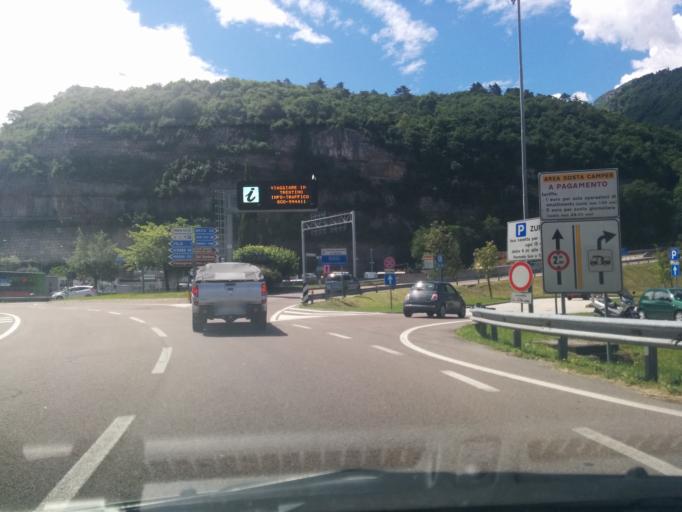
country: IT
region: Trentino-Alto Adige
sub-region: Provincia di Trento
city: Trento
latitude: 46.0766
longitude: 11.1113
